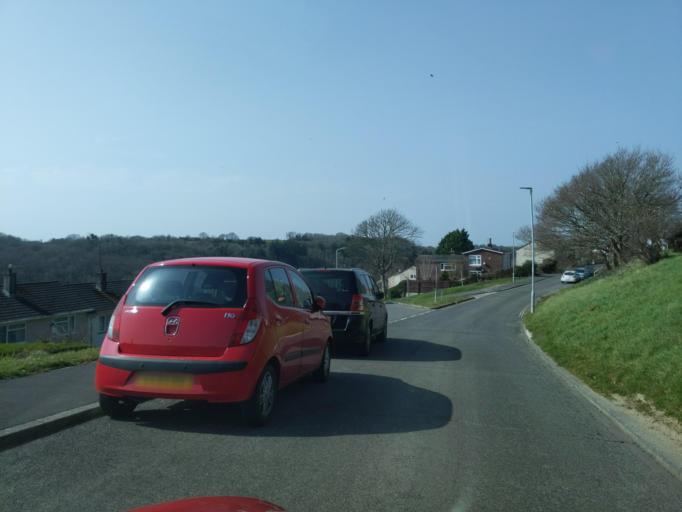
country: GB
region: England
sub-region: Plymouth
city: Plymouth
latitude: 50.4251
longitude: -4.1398
